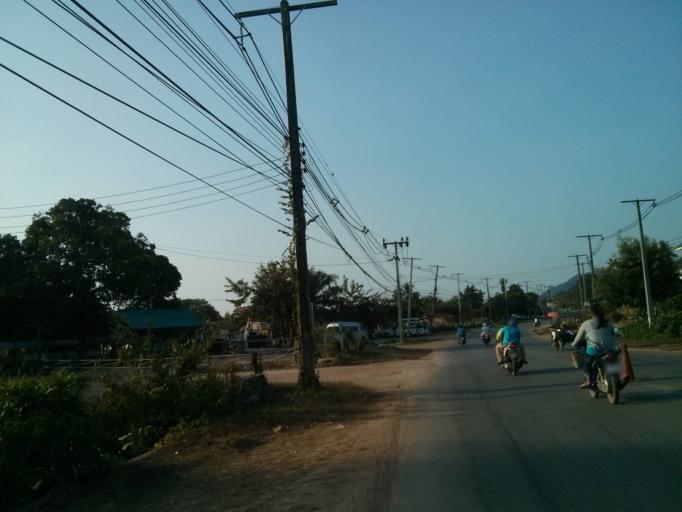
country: TH
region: Krabi
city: Saladan
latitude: 7.5896
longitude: 99.0354
